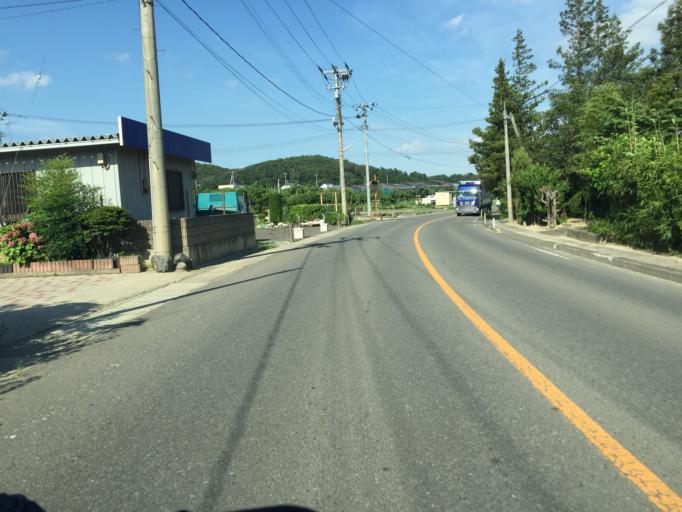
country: JP
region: Fukushima
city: Fukushima-shi
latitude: 37.8128
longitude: 140.4210
